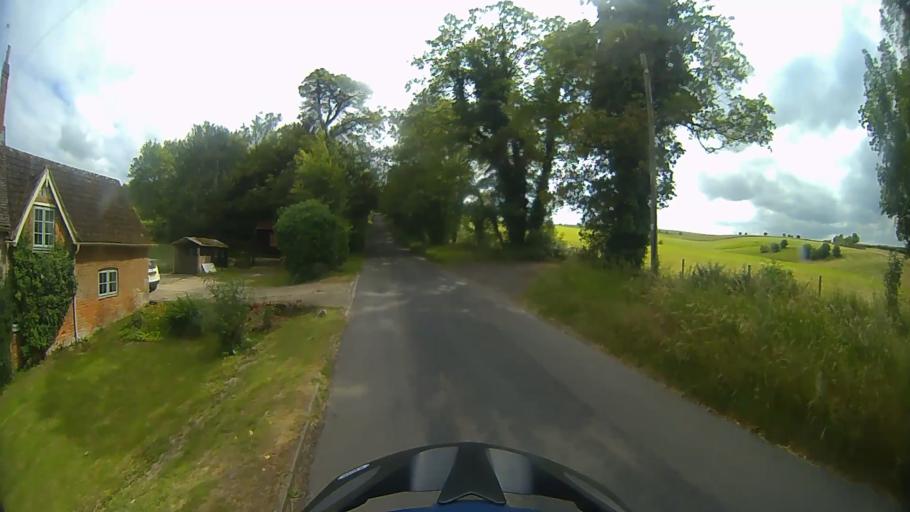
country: GB
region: England
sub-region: Oxfordshire
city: Stanford in the Vale
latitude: 51.5816
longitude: -1.5337
